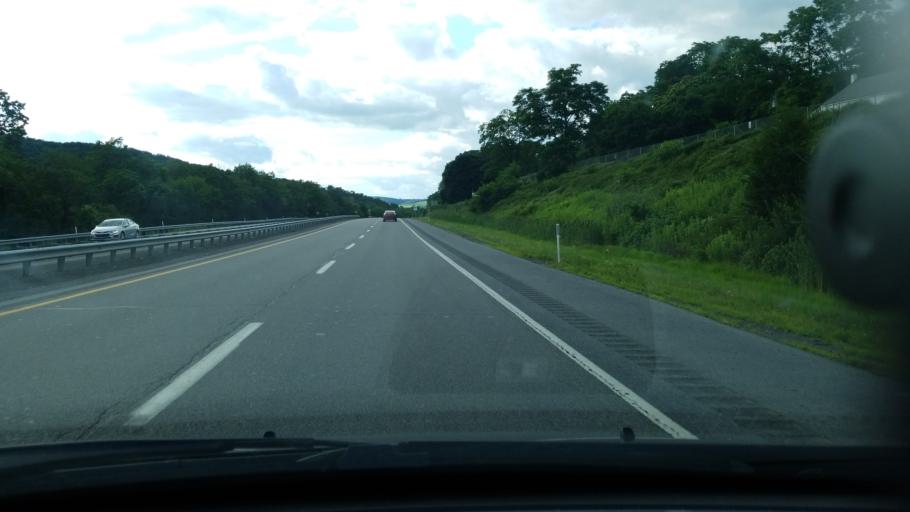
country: US
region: Pennsylvania
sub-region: Montour County
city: Danville
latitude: 40.9759
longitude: -76.6212
